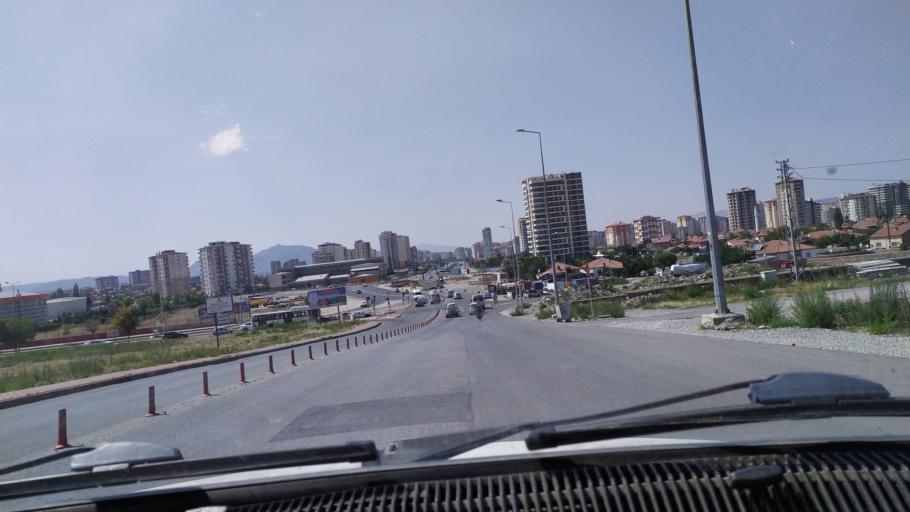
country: TR
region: Kayseri
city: Talas
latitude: 38.7199
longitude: 35.5522
